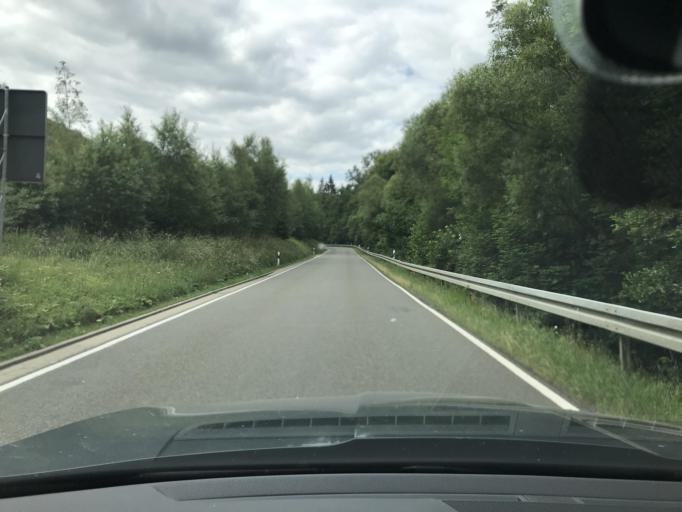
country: DE
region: Saxony-Anhalt
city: Harzgerode
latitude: 51.6422
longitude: 11.1064
